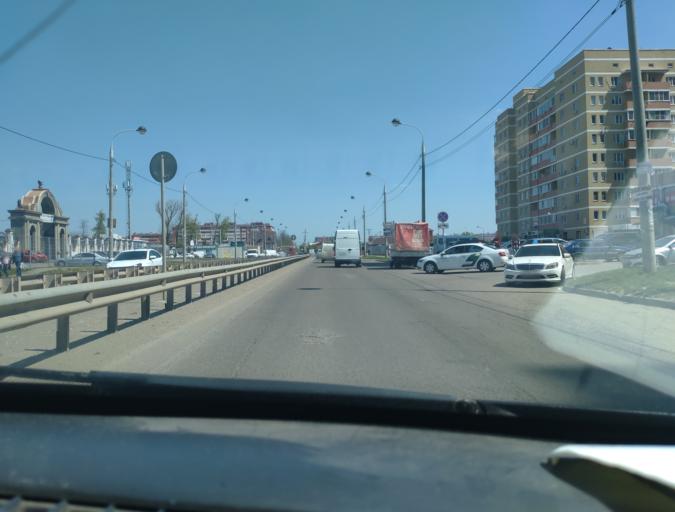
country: RU
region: Krasnodarskiy
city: Krasnodar
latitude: 45.0944
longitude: 39.0103
